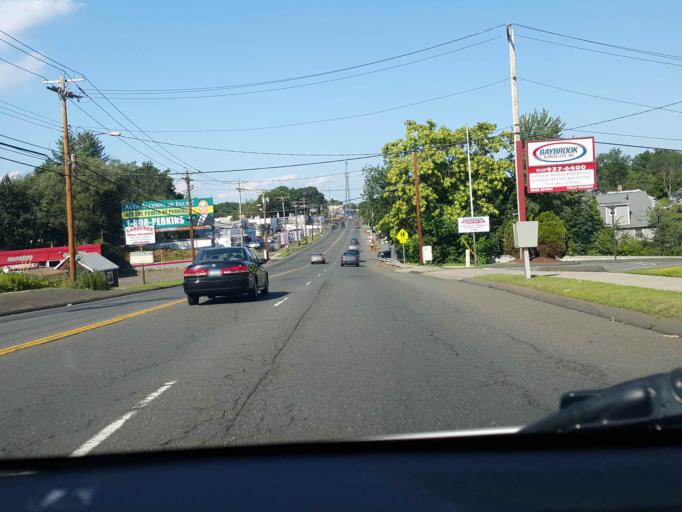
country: US
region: Connecticut
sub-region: New Haven County
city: West Haven
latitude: 41.2866
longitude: -72.9750
